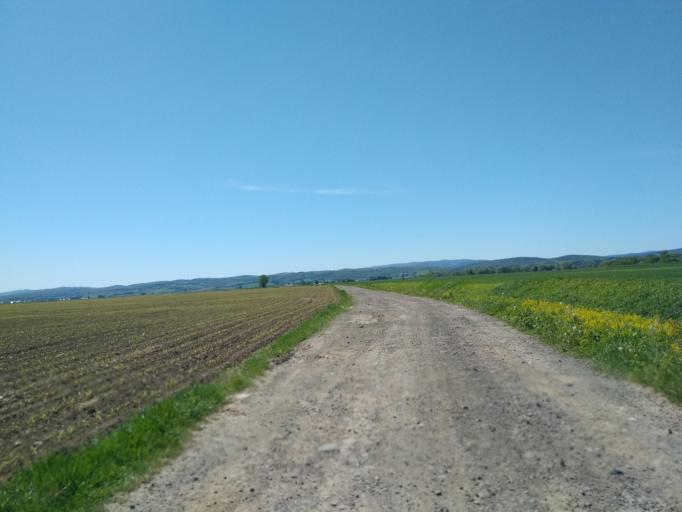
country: PL
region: Subcarpathian Voivodeship
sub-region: Powiat sanocki
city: Besko
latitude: 49.6184
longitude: 21.9716
